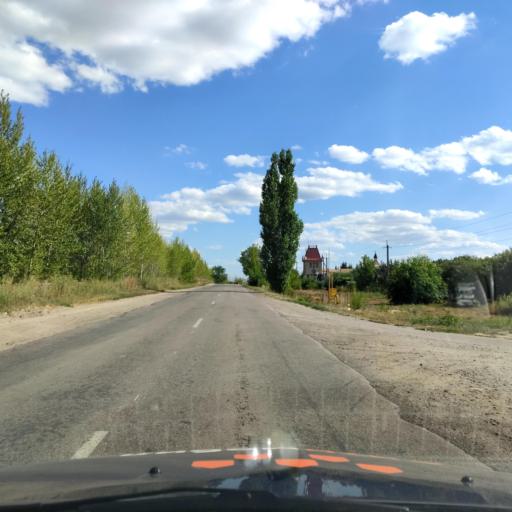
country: RU
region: Voronezj
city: Somovo
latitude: 51.7083
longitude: 39.3695
